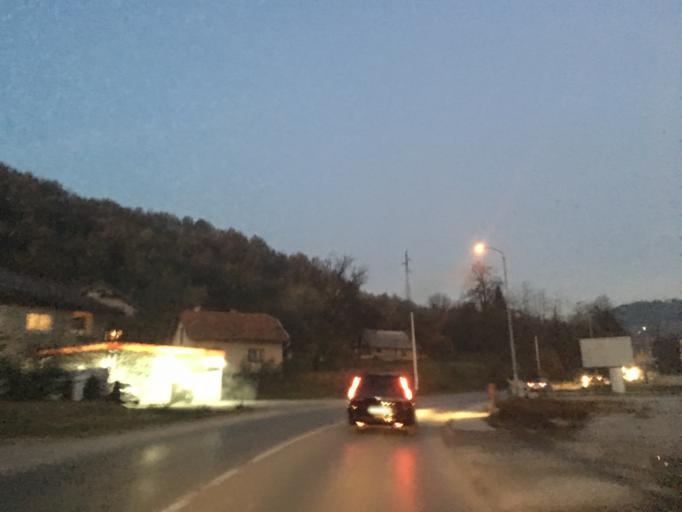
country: BA
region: Federation of Bosnia and Herzegovina
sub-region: Kanton Sarajevo
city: Sarajevo
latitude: 43.8376
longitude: 18.3877
